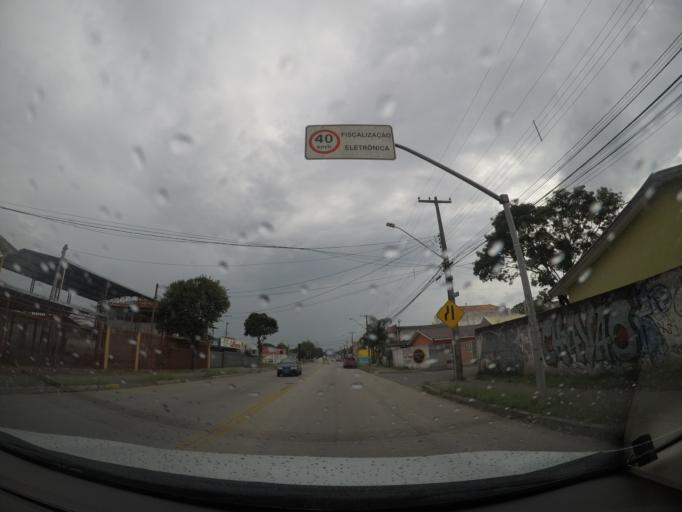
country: BR
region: Parana
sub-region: Sao Jose Dos Pinhais
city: Sao Jose dos Pinhais
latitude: -25.5086
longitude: -49.2177
